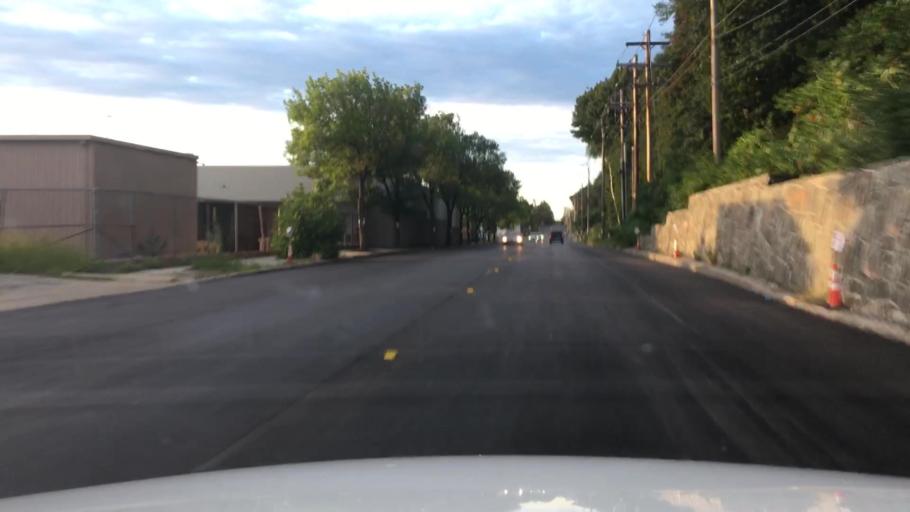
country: US
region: Maine
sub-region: Cumberland County
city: Portland
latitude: 43.6462
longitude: -70.2771
